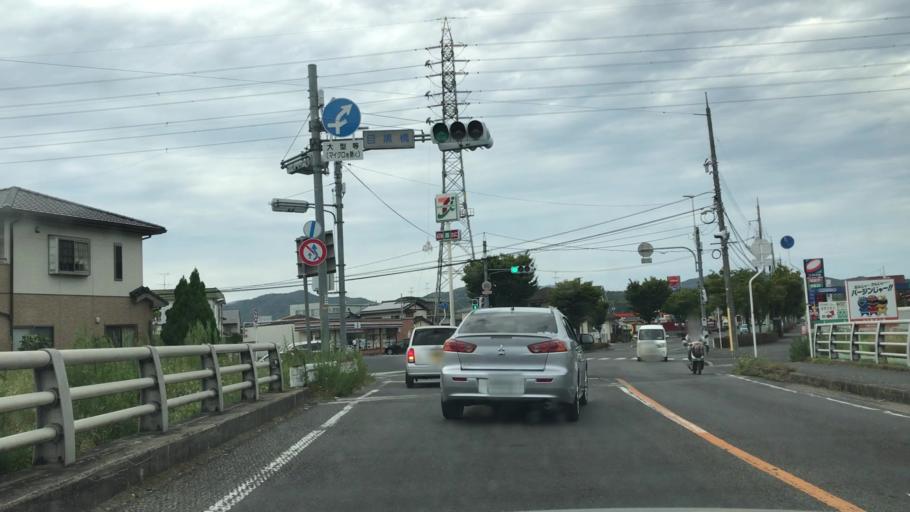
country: JP
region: Okayama
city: Okayama-shi
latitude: 34.6708
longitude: 133.9988
